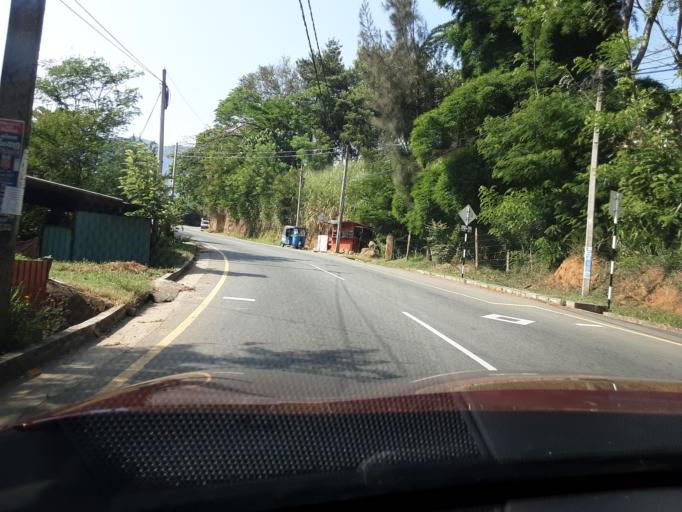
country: LK
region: Uva
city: Badulla
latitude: 6.9856
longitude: 81.0783
